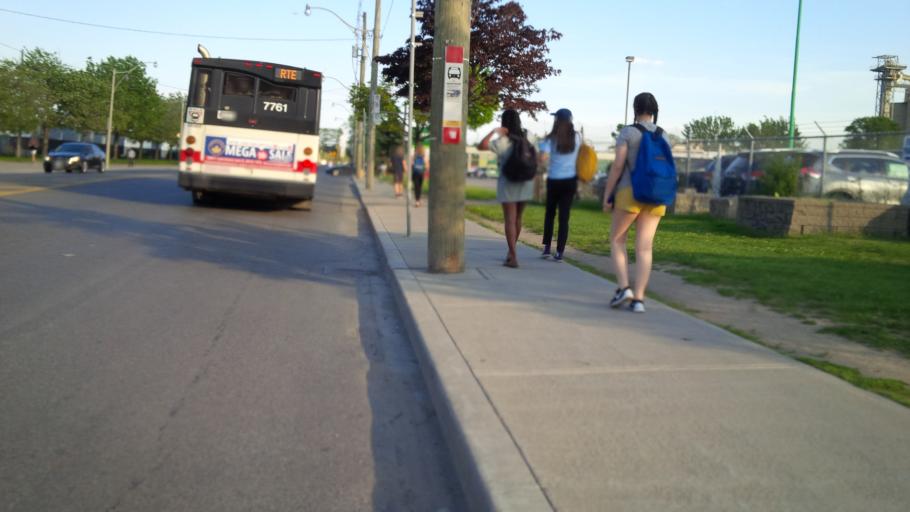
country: CA
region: Ontario
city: Toronto
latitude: 43.6450
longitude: -79.3523
